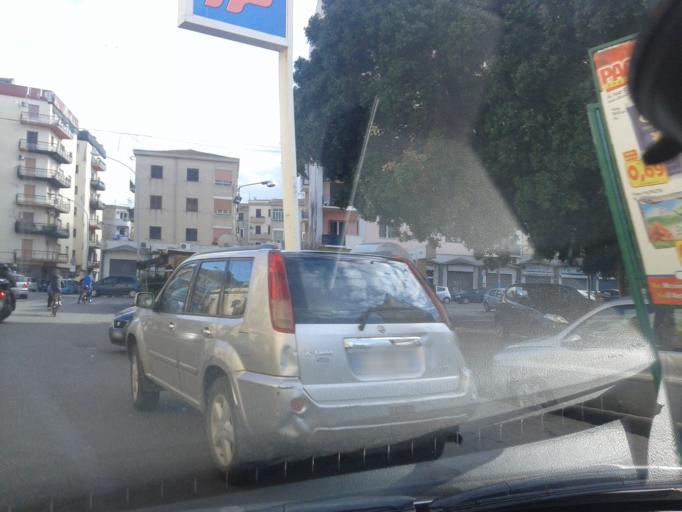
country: IT
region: Sicily
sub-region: Palermo
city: Palermo
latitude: 38.1167
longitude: 13.3447
